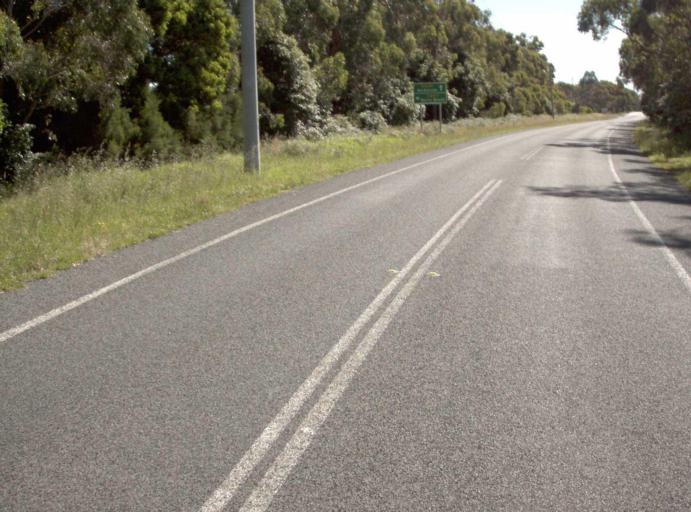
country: AU
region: Victoria
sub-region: Latrobe
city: Morwell
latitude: -38.6685
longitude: 146.4017
